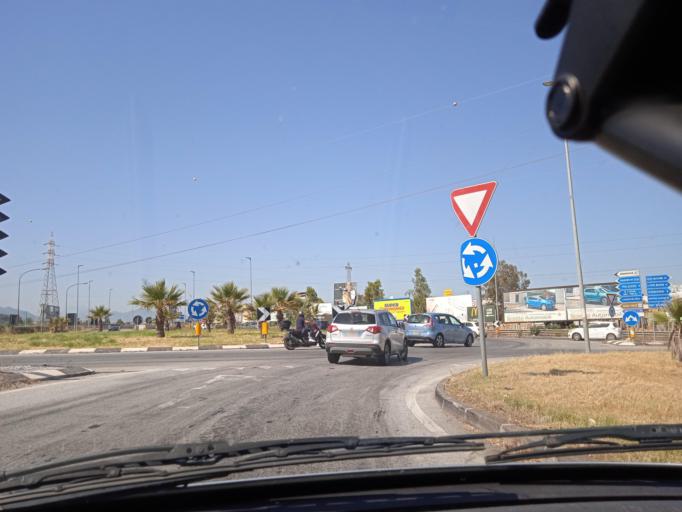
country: IT
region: Sicily
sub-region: Messina
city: San Filippo del Mela
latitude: 38.1888
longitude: 15.2736
